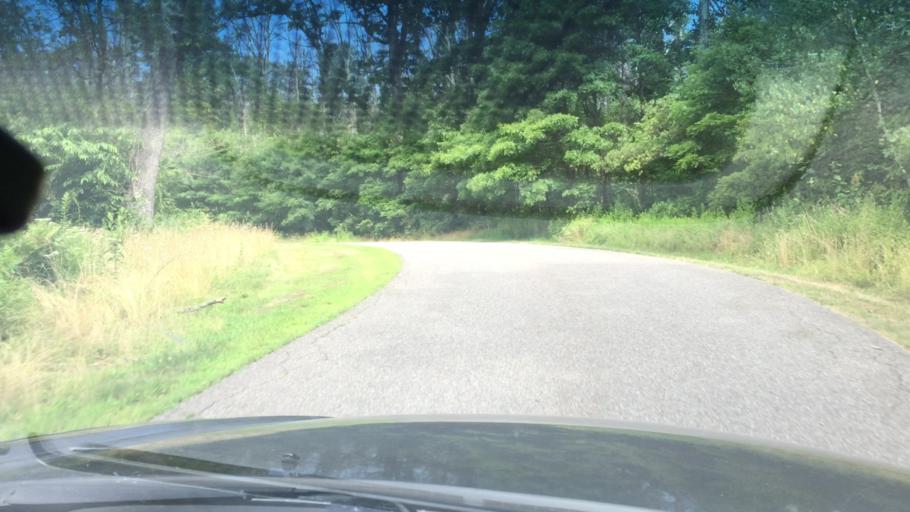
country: US
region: Pennsylvania
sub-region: Luzerne County
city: Harleigh
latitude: 41.0392
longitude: -75.9767
